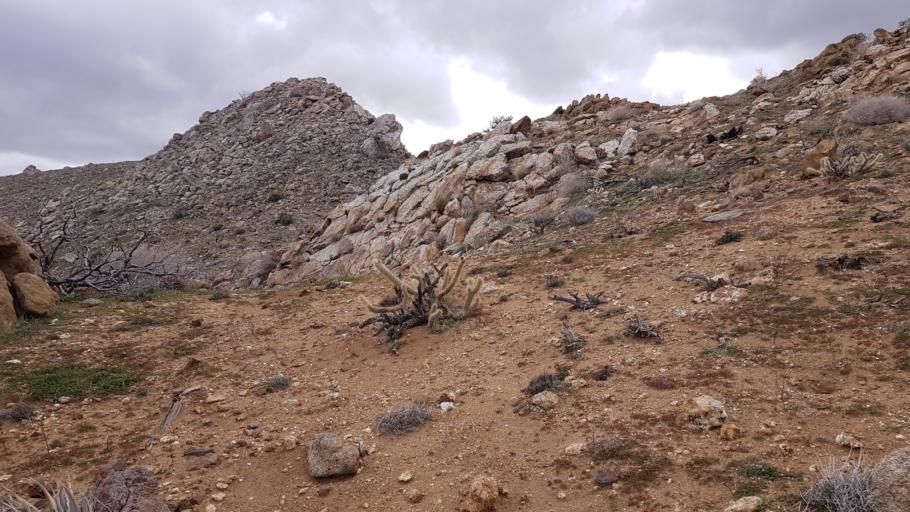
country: US
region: California
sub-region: San Diego County
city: Julian
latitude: 33.1240
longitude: -116.4651
